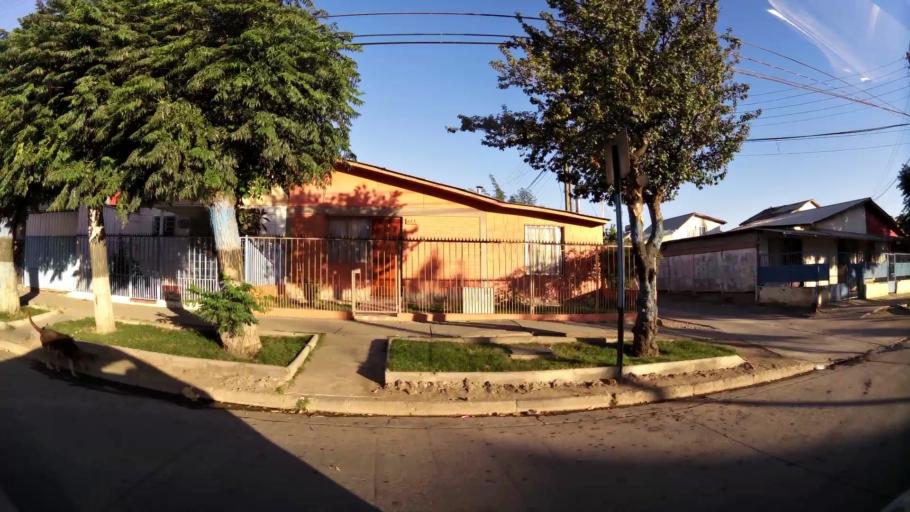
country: CL
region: O'Higgins
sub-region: Provincia de Cachapoal
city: Rancagua
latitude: -34.1702
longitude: -70.7614
